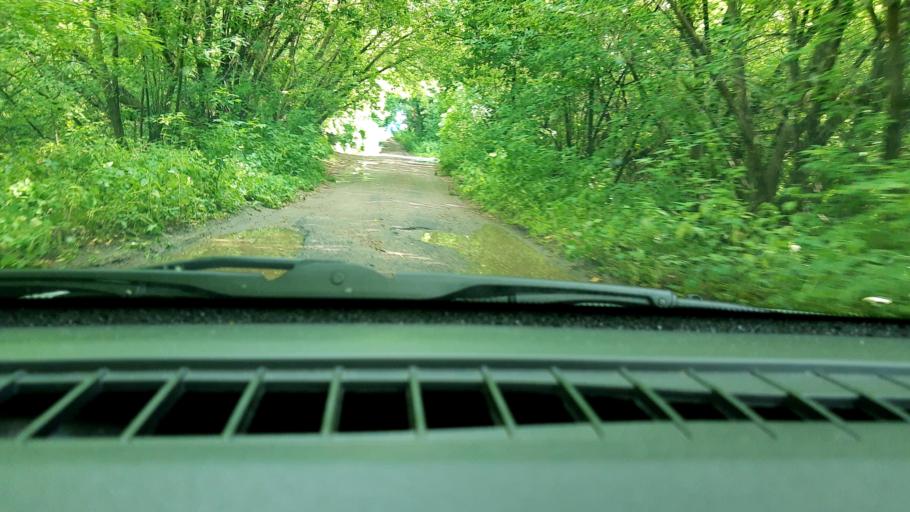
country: RU
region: Nizjnij Novgorod
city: Neklyudovo
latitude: 56.3965
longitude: 43.8497
